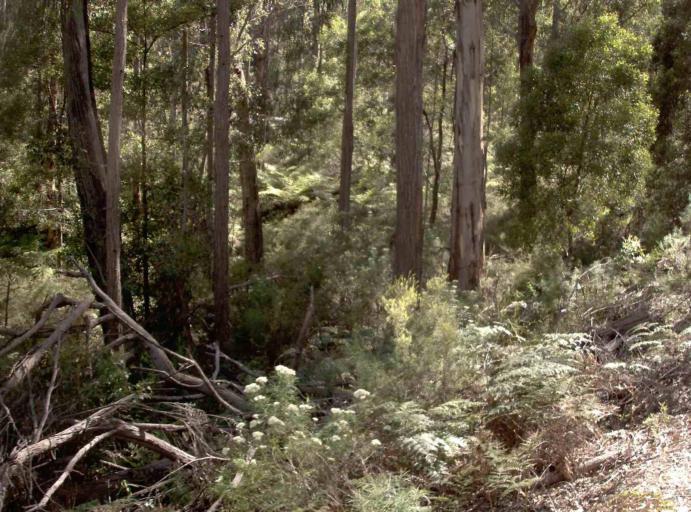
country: AU
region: New South Wales
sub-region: Bombala
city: Bombala
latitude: -37.2810
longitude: 148.7187
